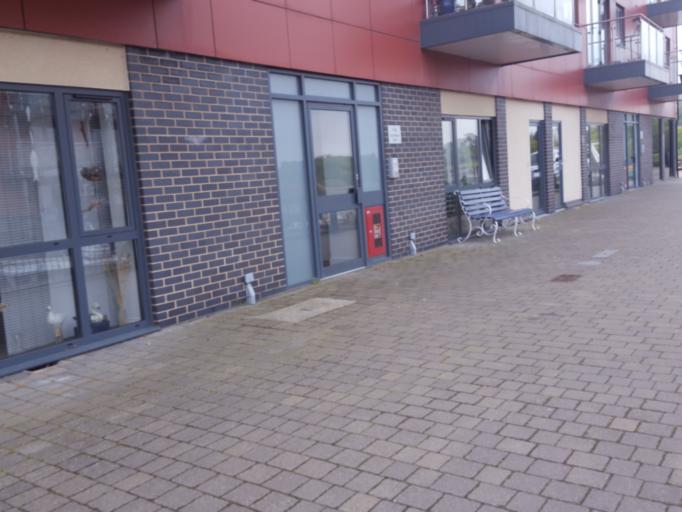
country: GB
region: England
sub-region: Essex
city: Wivenhoe
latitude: 51.8541
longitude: 0.9616
